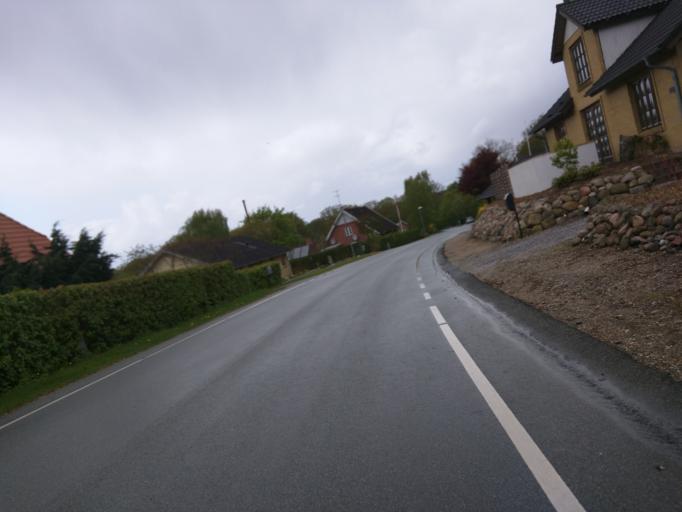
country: DK
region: Central Jutland
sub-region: Viborg Kommune
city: Viborg
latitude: 56.3992
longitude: 9.4355
